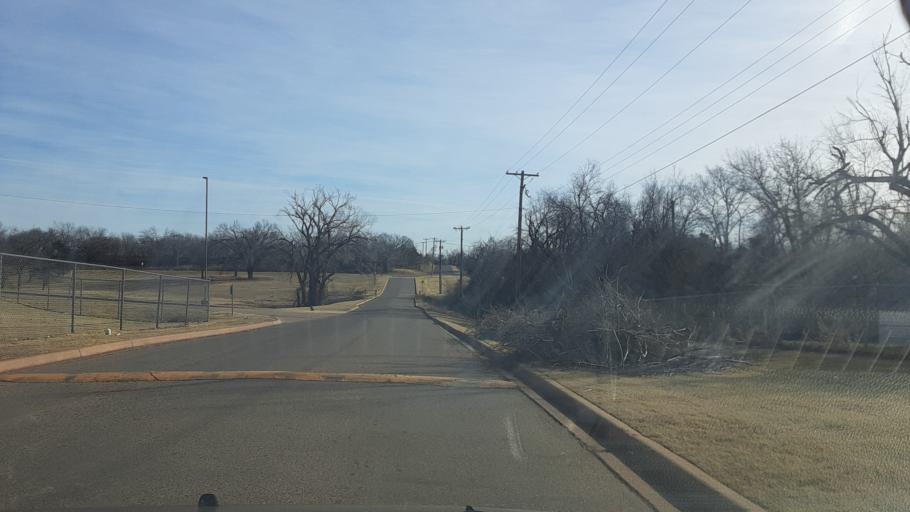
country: US
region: Oklahoma
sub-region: Logan County
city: Guthrie
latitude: 35.8926
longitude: -97.4188
